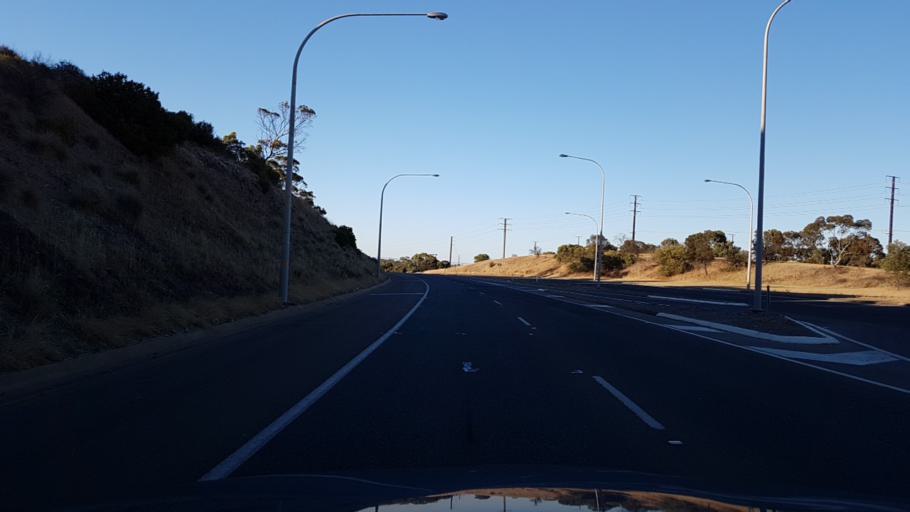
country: AU
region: South Australia
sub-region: Onkaparinga
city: Morphett Vale
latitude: -35.1130
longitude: 138.4921
